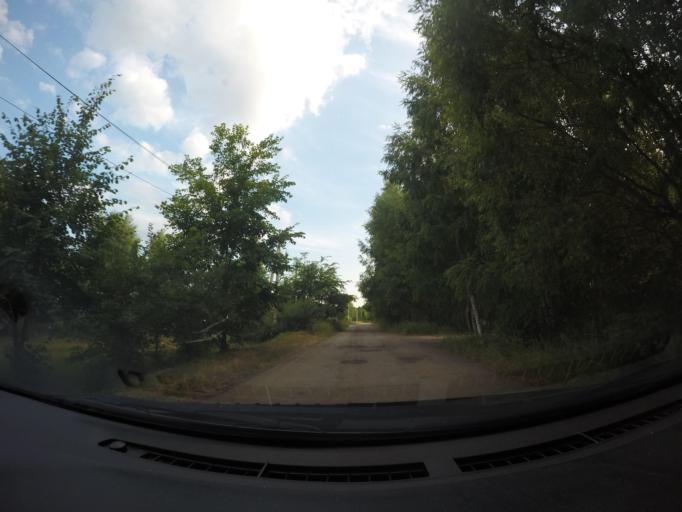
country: RU
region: Moskovskaya
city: Krasnyy Tkach
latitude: 55.4219
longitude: 39.2375
